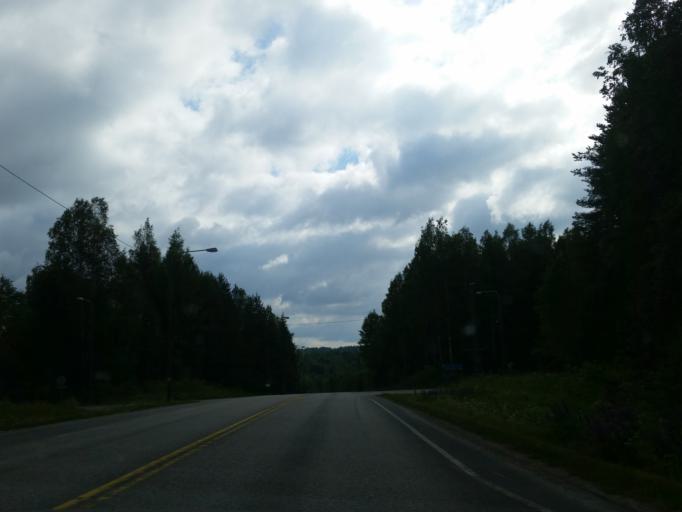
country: FI
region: Northern Savo
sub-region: Sisae-Savo
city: Suonenjoki
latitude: 62.8429
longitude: 27.3401
